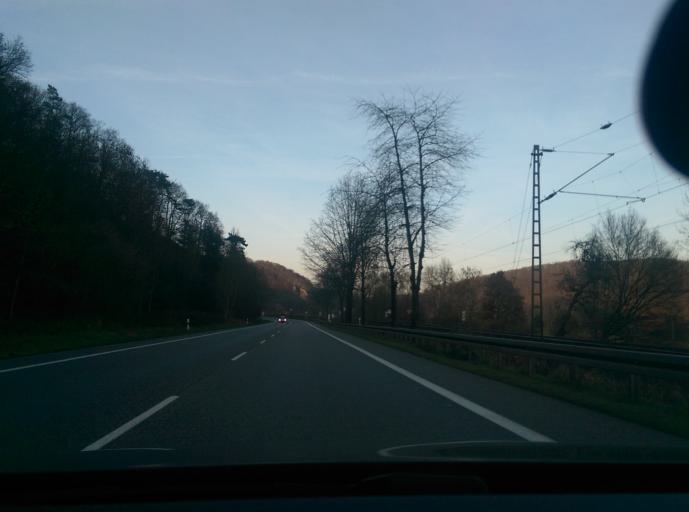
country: DE
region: Hesse
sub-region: Regierungsbezirk Kassel
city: Bad Sooden-Allendorf
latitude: 51.2285
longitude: 9.9908
